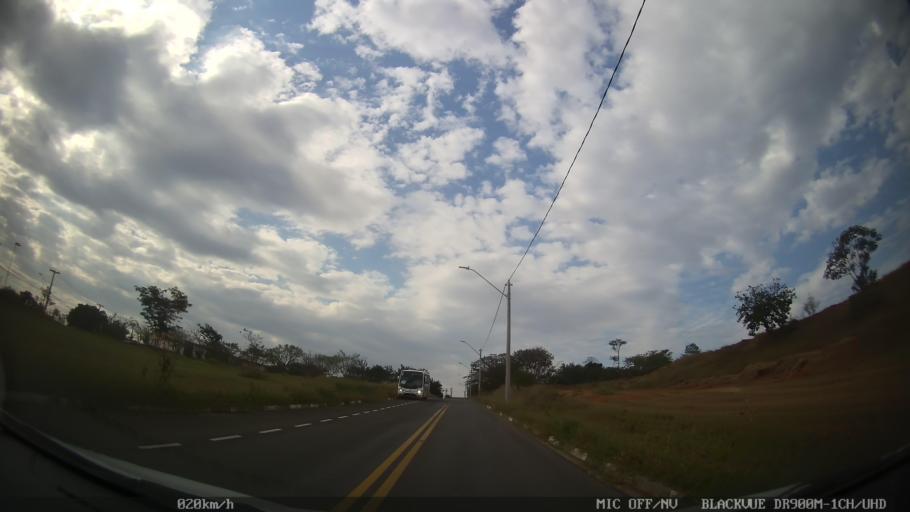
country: BR
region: Sao Paulo
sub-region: Paulinia
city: Paulinia
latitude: -22.7377
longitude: -47.1735
